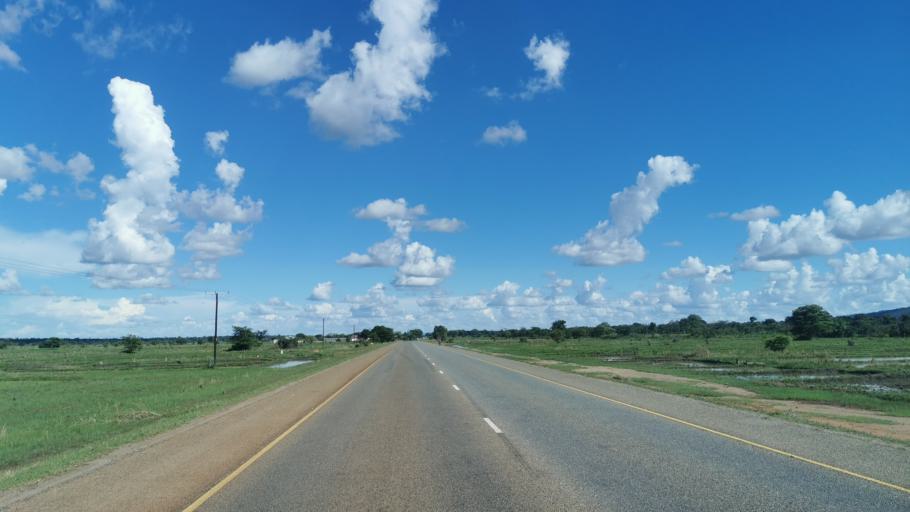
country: TZ
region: Geita
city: Ushirombo
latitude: -3.4806
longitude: 31.9246
